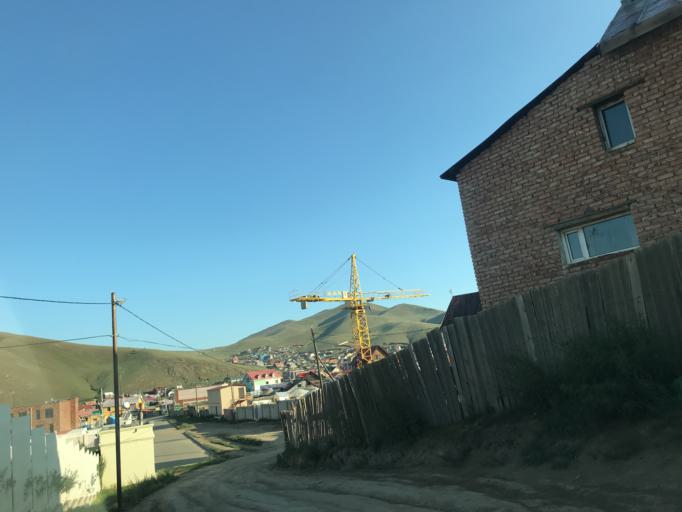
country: MN
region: Ulaanbaatar
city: Ulaanbaatar
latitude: 47.9947
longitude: 106.9688
